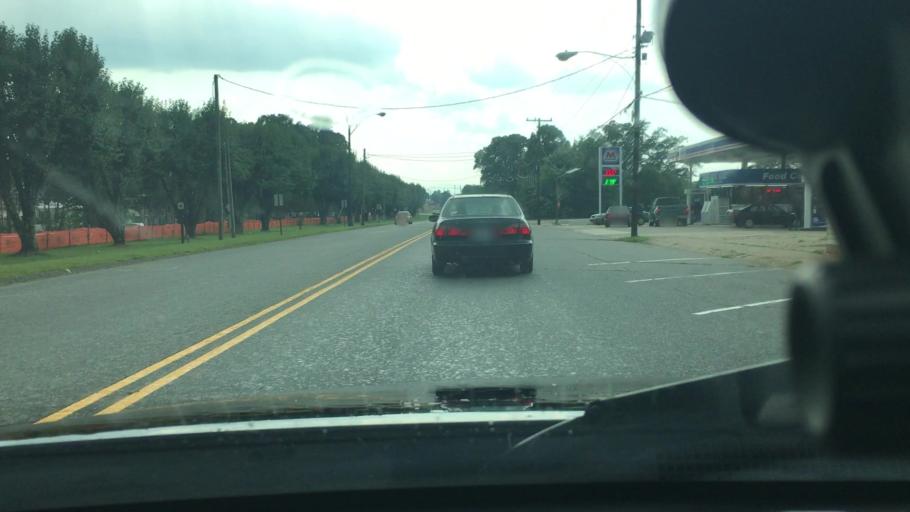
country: US
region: North Carolina
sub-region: Rutherford County
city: Spindale
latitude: 35.3554
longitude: -81.9249
